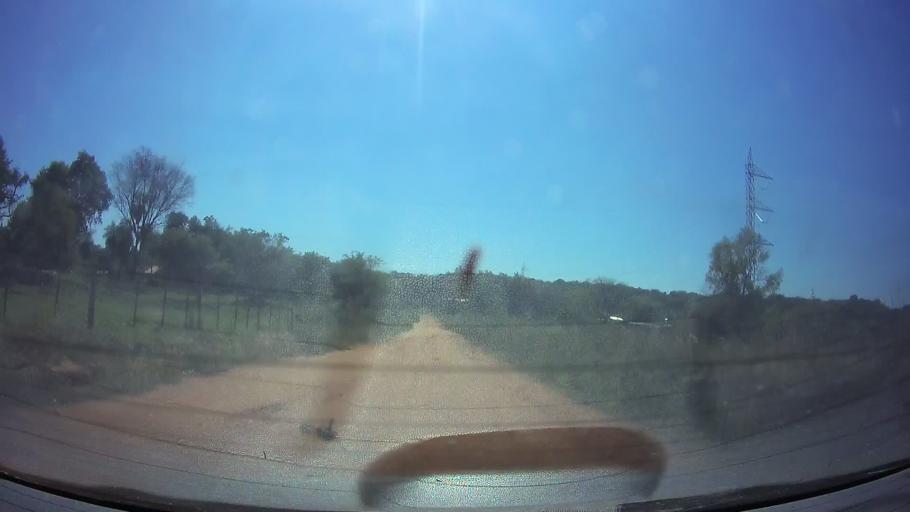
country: PY
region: Central
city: Limpio
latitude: -25.2388
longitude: -57.4414
